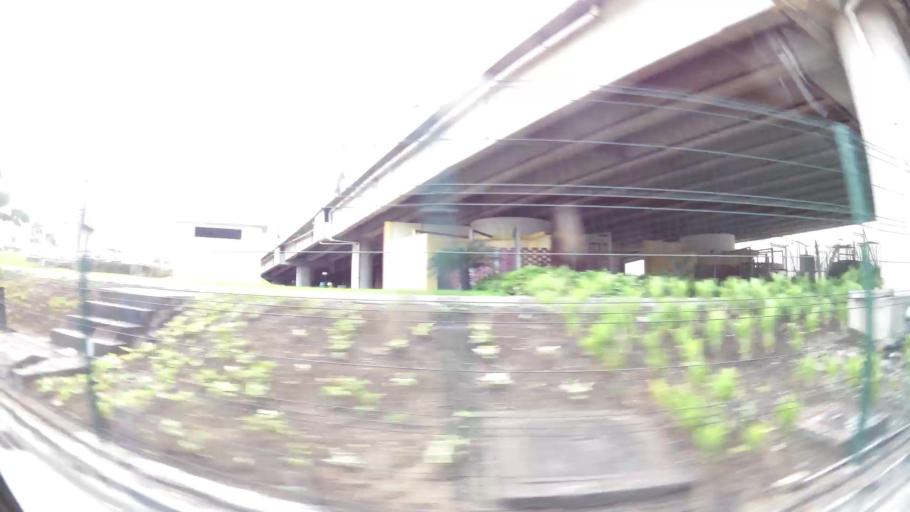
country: EC
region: Guayas
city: Eloy Alfaro
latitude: -2.1400
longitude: -79.8825
